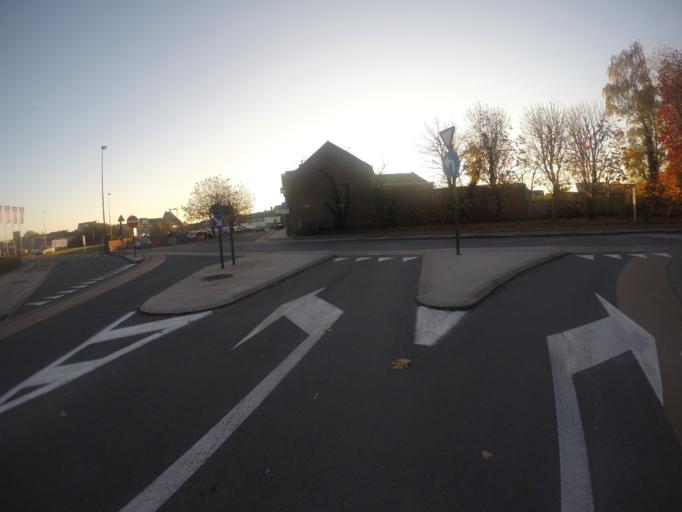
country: BE
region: Flanders
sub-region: Provincie Oost-Vlaanderen
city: Aalter
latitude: 51.0939
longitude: 3.4472
